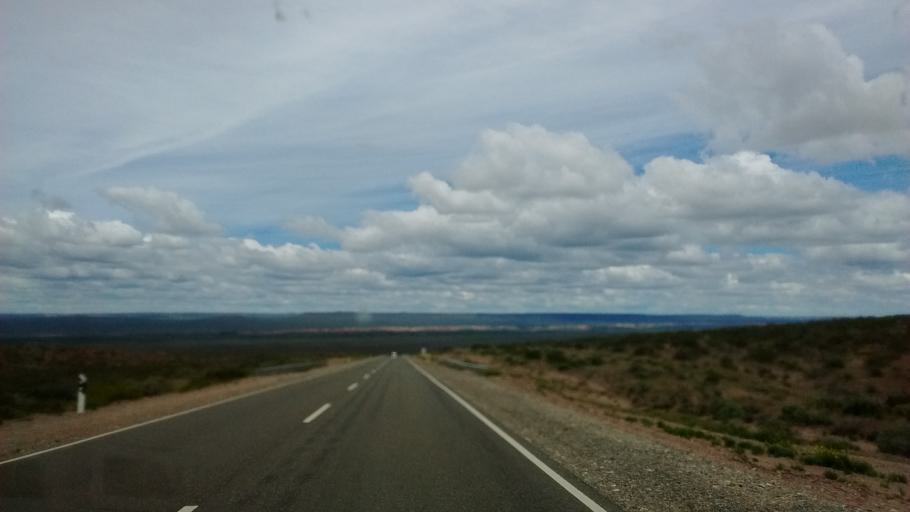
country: AR
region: Neuquen
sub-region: Departamento de Picun Leufu
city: Picun Leufu
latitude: -39.7652
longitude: -69.6505
